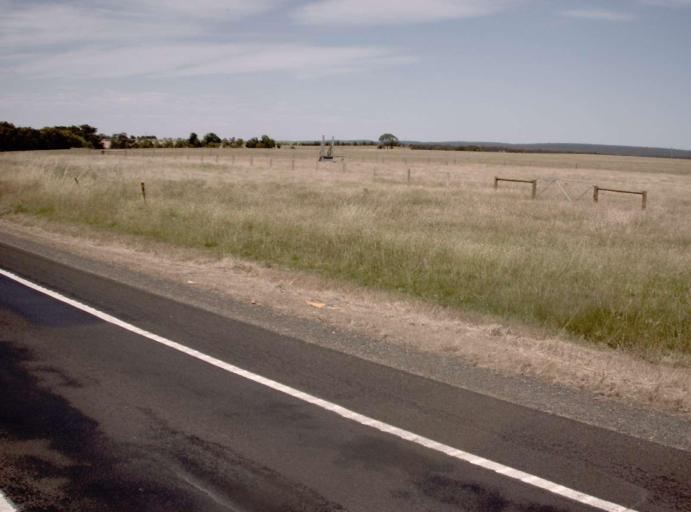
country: AU
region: Victoria
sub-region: Wellington
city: Heyfield
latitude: -38.1319
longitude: 146.8135
